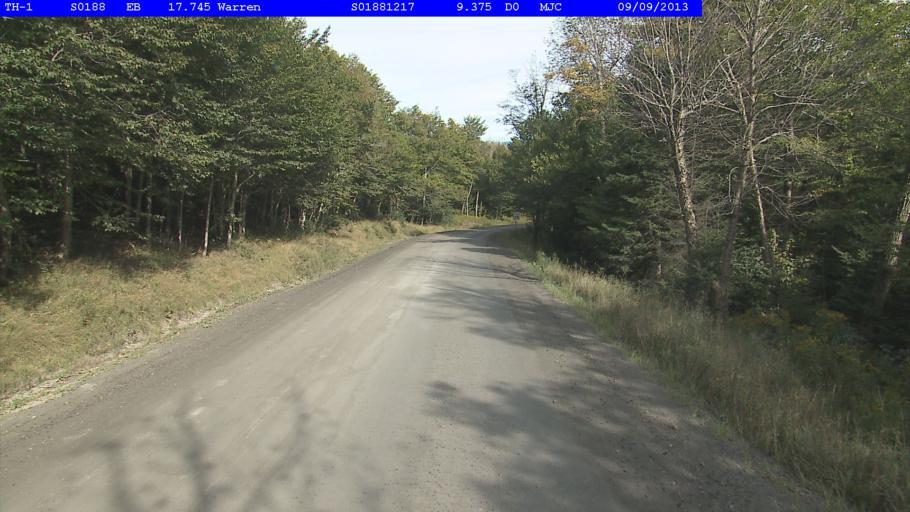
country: US
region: Vermont
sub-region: Washington County
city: Northfield
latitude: 44.1136
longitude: -72.7815
